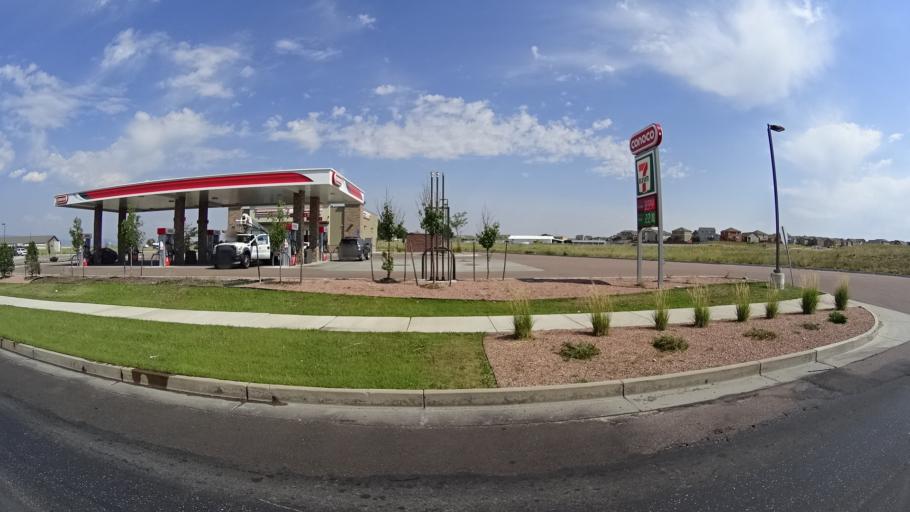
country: US
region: Colorado
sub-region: El Paso County
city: Cimarron Hills
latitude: 38.9259
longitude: -104.7142
